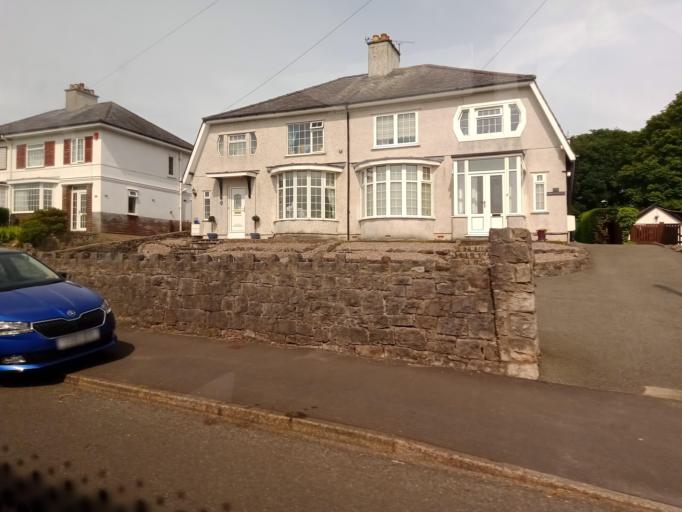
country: GB
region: Wales
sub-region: Gwynedd
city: Bangor
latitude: 53.2183
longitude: -4.1464
